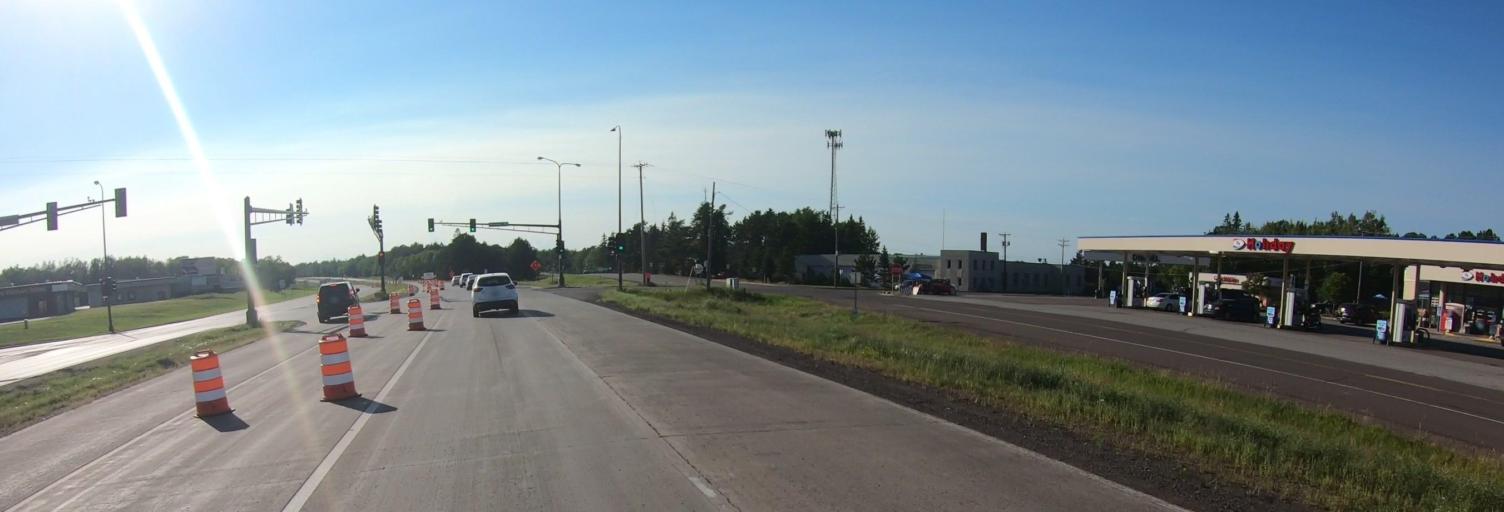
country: US
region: Minnesota
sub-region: Saint Louis County
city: Hermantown
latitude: 46.8504
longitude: -92.2827
